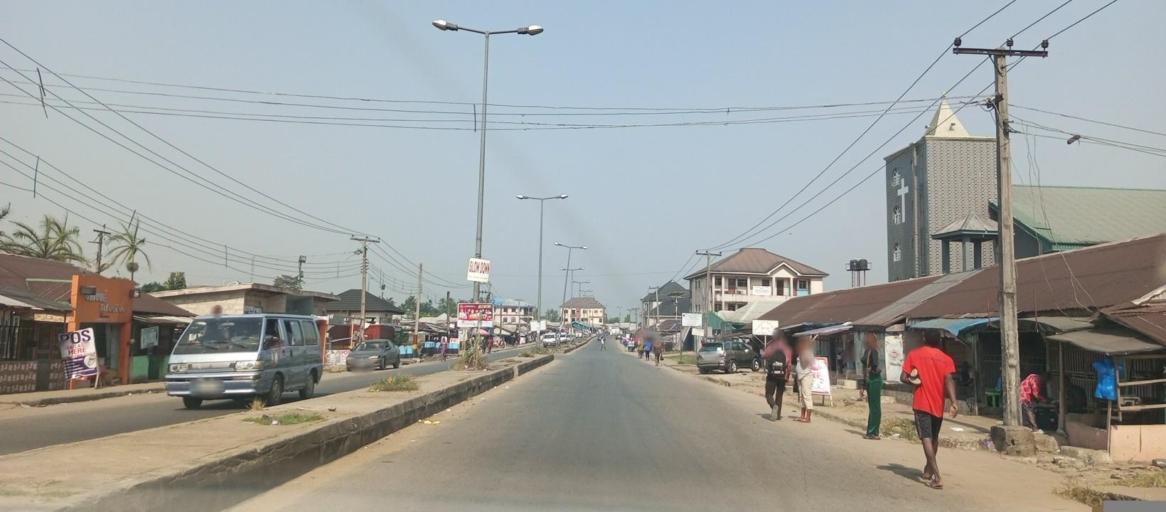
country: NG
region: Rivers
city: Emuoha
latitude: 4.8843
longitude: 6.9038
